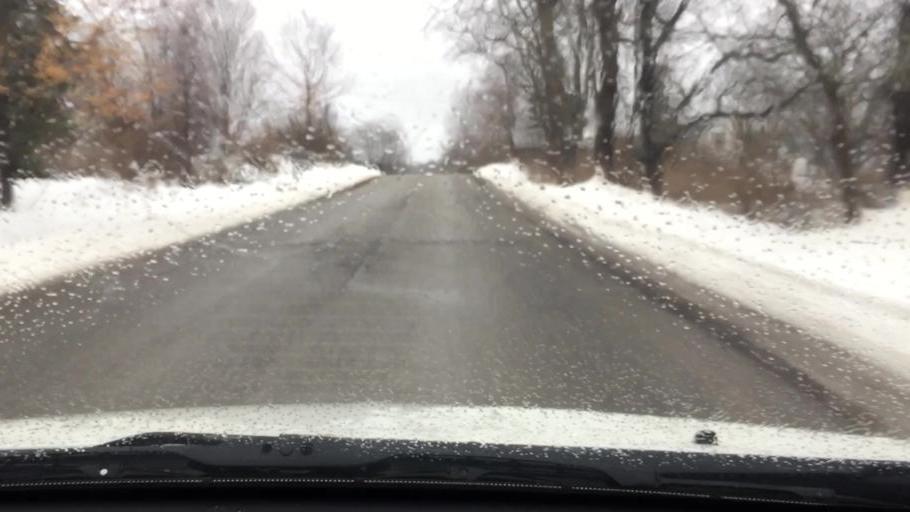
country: US
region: Michigan
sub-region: Charlevoix County
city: East Jordan
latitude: 45.1056
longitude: -85.1520
